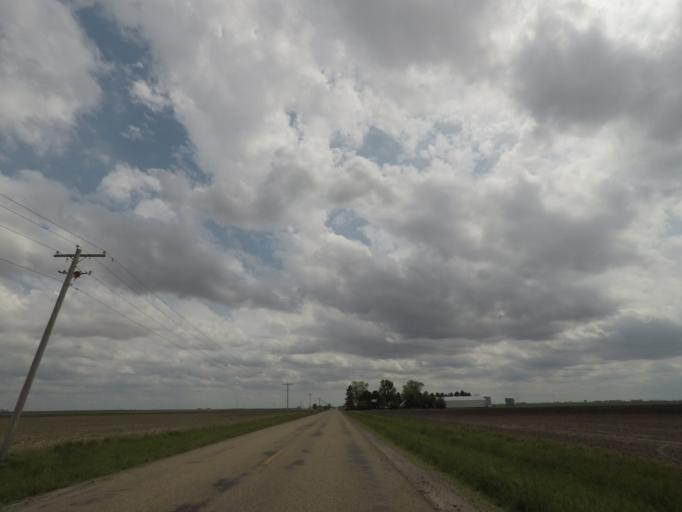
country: US
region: Illinois
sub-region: Macon County
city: Maroa
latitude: 40.0842
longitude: -89.0859
